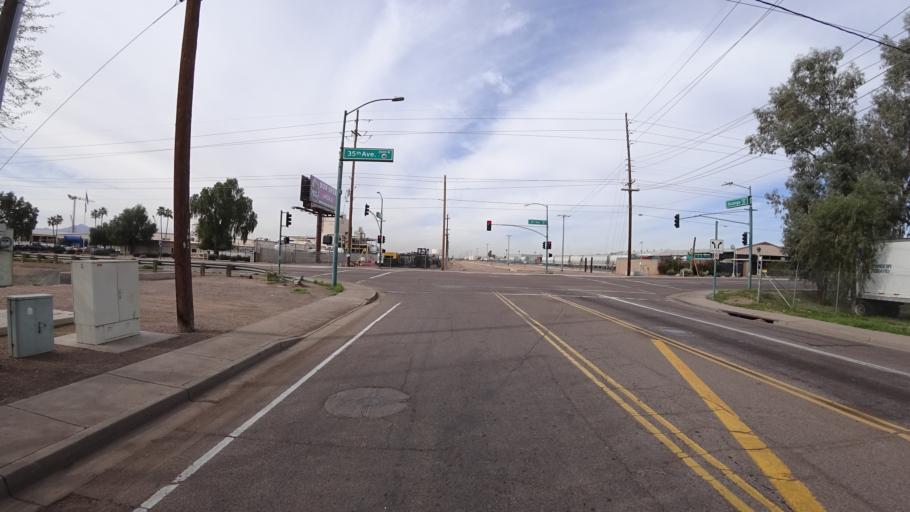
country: US
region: Arizona
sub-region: Maricopa County
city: Phoenix
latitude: 33.4296
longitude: -112.1343
